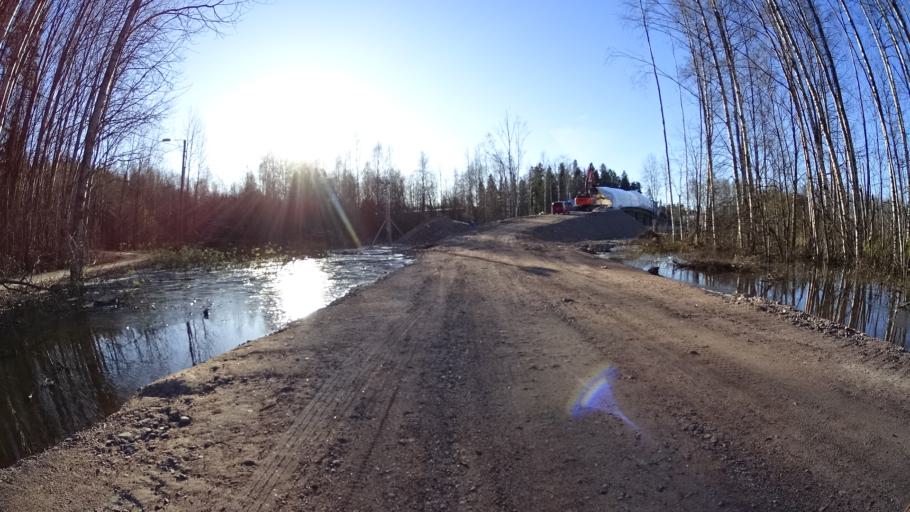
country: FI
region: Uusimaa
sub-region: Helsinki
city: Espoo
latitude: 60.2129
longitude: 24.6765
